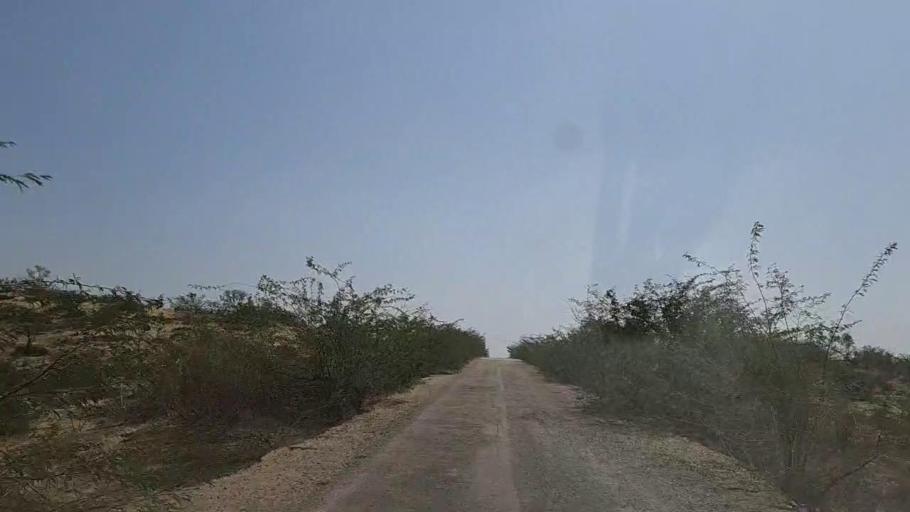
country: PK
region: Sindh
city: Diplo
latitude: 24.4973
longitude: 69.4310
